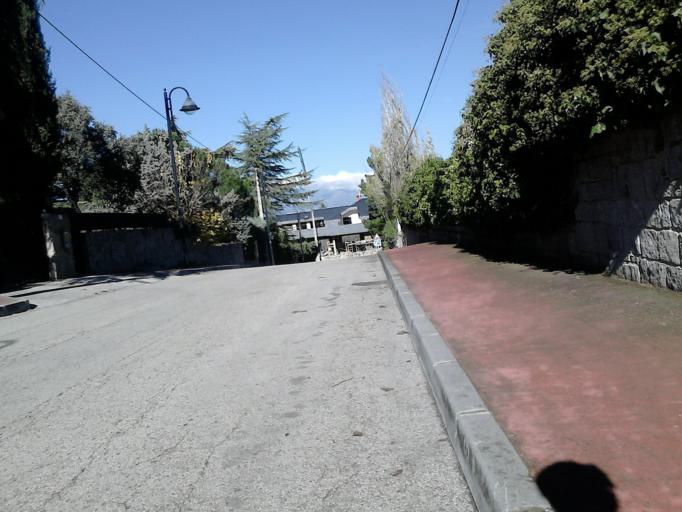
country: ES
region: Madrid
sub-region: Provincia de Madrid
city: Galapagar
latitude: 40.5721
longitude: -3.9963
